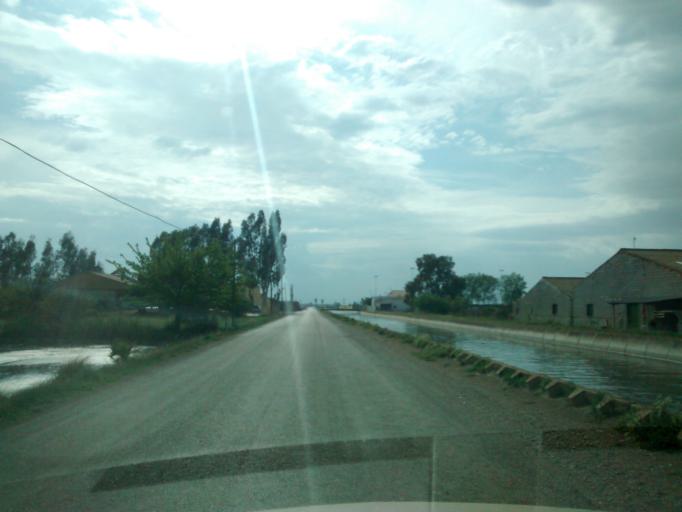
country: ES
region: Catalonia
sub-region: Provincia de Tarragona
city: Deltebre
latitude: 40.7025
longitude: 0.7365
